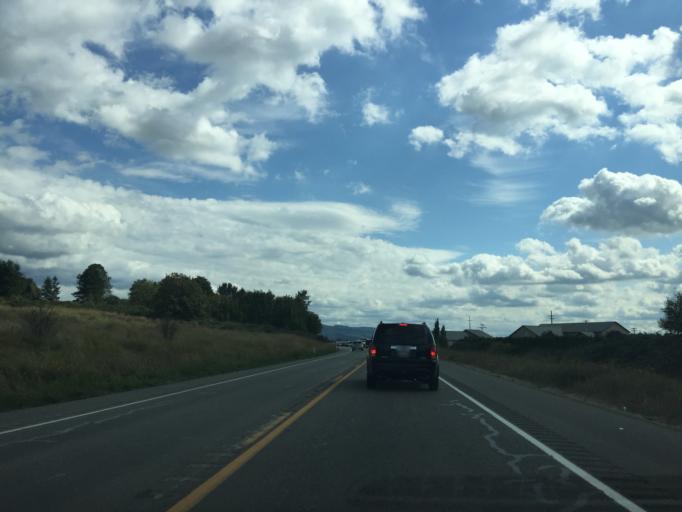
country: US
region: Washington
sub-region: Snohomish County
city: Monroe
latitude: 47.8781
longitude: -122.0177
